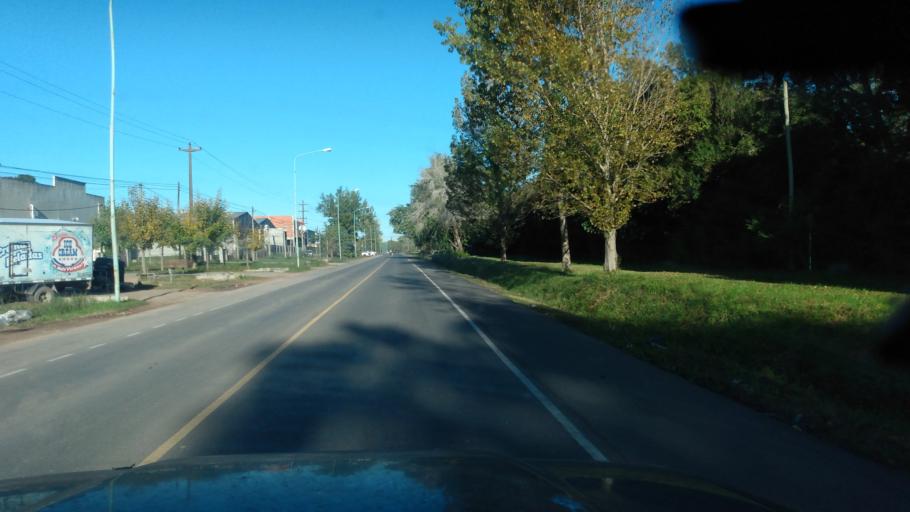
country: AR
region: Buenos Aires
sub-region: Partido de Lujan
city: Lujan
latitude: -34.5610
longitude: -59.1353
